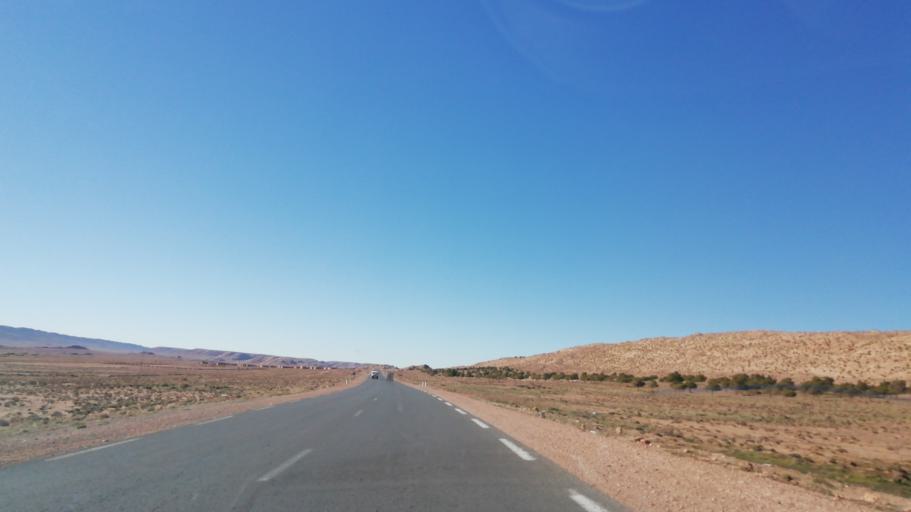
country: DZ
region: El Bayadh
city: El Bayadh
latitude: 33.6170
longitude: 1.1856
